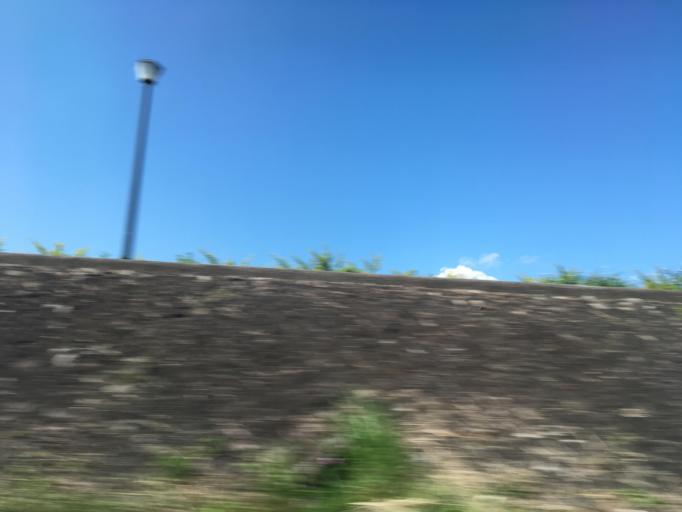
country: TW
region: Taiwan
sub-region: Yilan
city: Yilan
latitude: 24.7561
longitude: 121.7322
